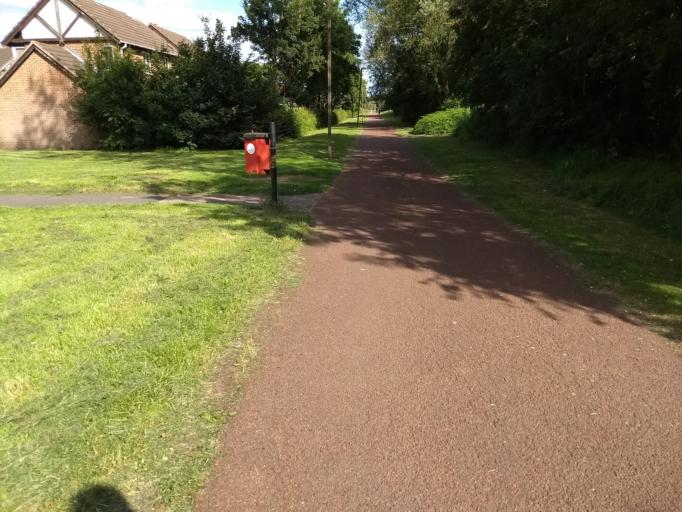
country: GB
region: England
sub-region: Milton Keynes
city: Shenley Church End
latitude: 52.0340
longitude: -0.8026
